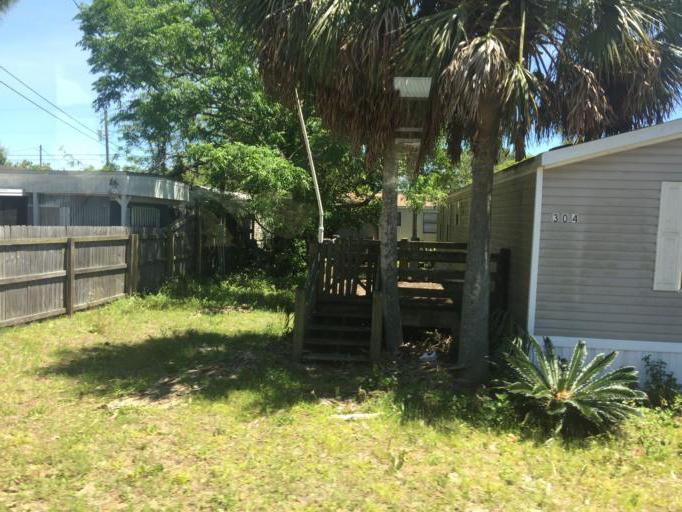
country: US
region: Florida
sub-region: Bay County
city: Laguna Beach
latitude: 30.2412
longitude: -85.9185
